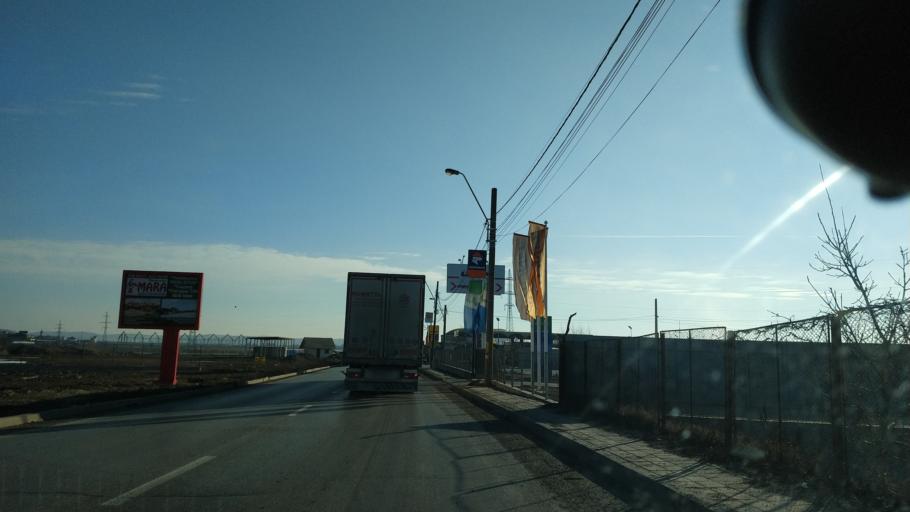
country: RO
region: Neamt
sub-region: Municipiul Roman
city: Roman
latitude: 46.9260
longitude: 26.9089
